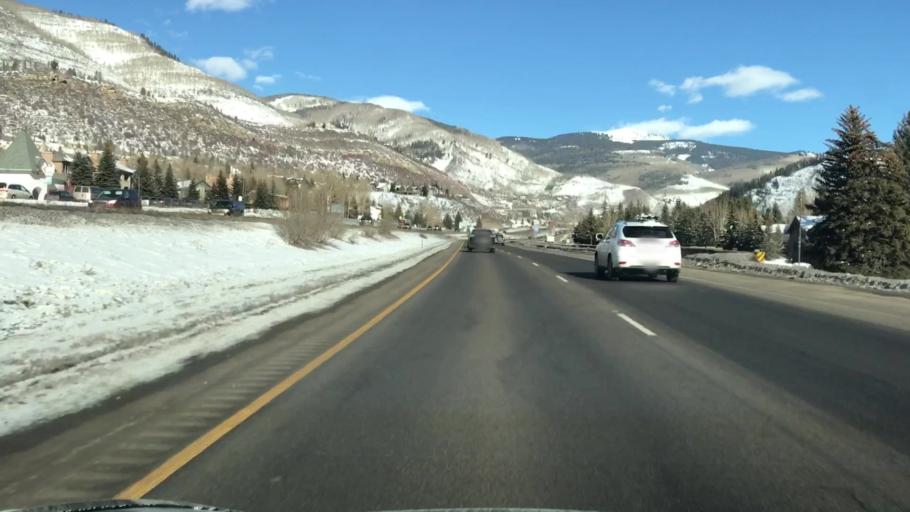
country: US
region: Colorado
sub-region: Eagle County
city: Vail
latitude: 39.6306
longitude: -106.4164
